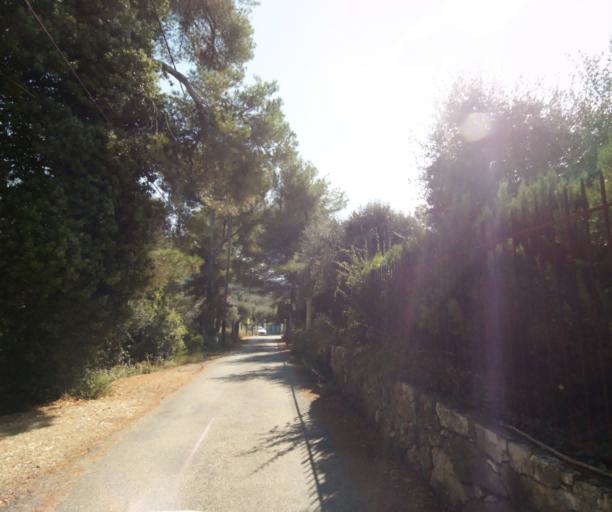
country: FR
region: Provence-Alpes-Cote d'Azur
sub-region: Departement des Alpes-Maritimes
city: Drap
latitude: 43.7519
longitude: 7.3404
